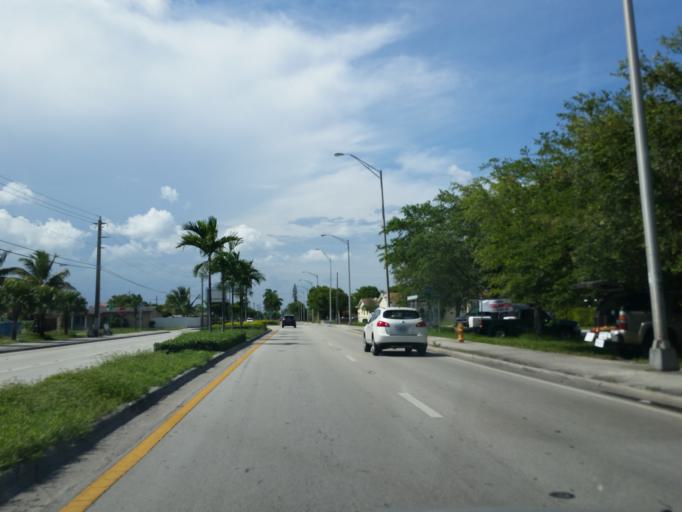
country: US
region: Florida
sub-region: Miami-Dade County
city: Westchester
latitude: 25.7501
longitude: -80.3357
